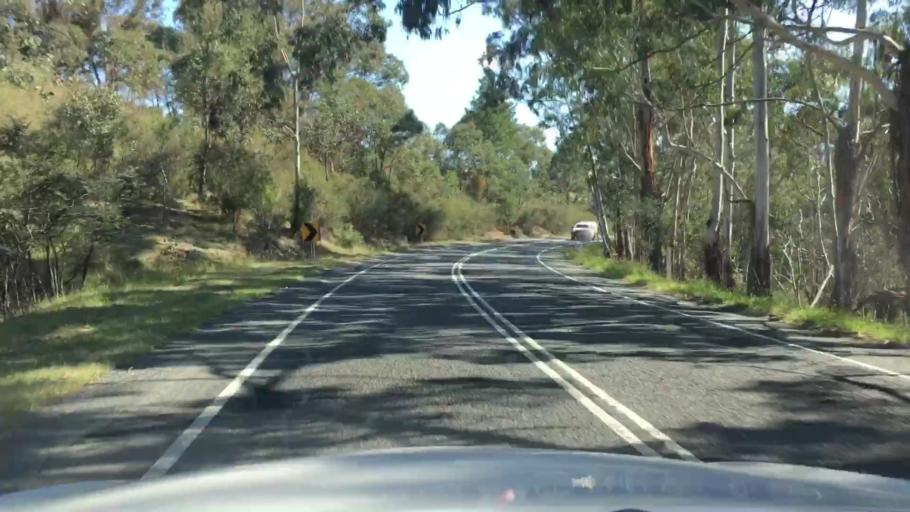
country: AU
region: Victoria
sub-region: Nillumbik
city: Saint Andrews
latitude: -37.6564
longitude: 145.2750
